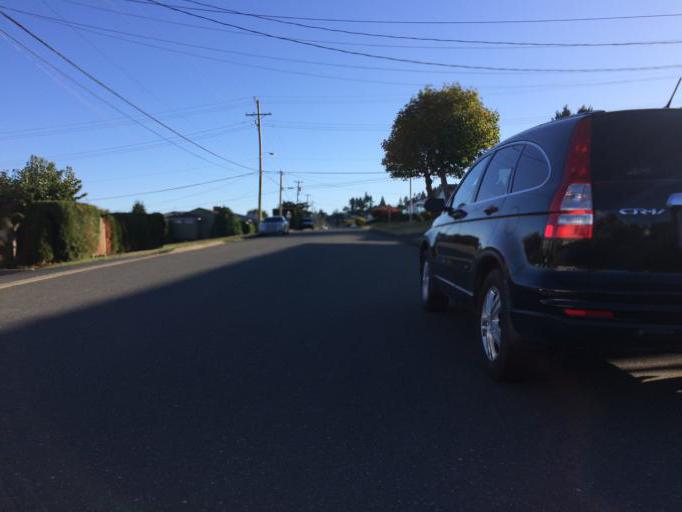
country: CA
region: British Columbia
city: Campbell River
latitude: 50.0082
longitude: -125.2369
